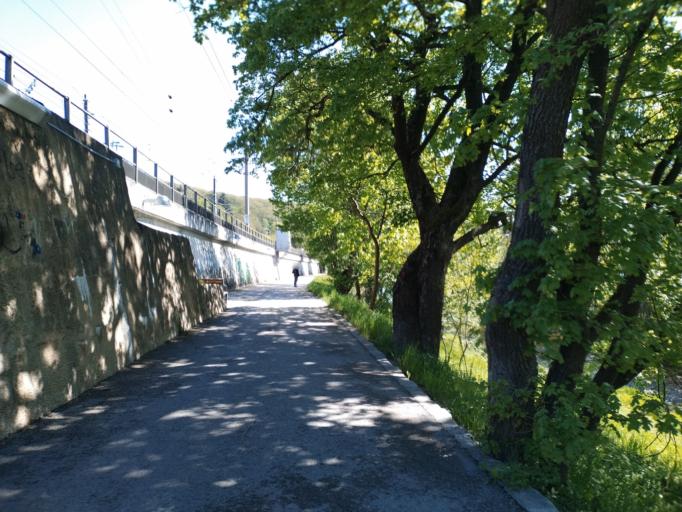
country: AT
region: Lower Austria
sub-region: Politischer Bezirk Wien-Umgebung
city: Purkersdorf
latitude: 48.2093
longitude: 16.2089
